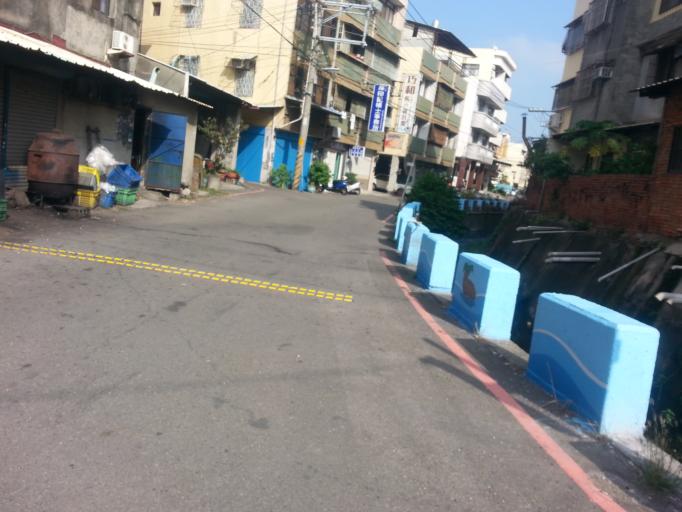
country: TW
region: Taiwan
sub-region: Changhua
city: Chang-hua
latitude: 24.0903
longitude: 120.5481
